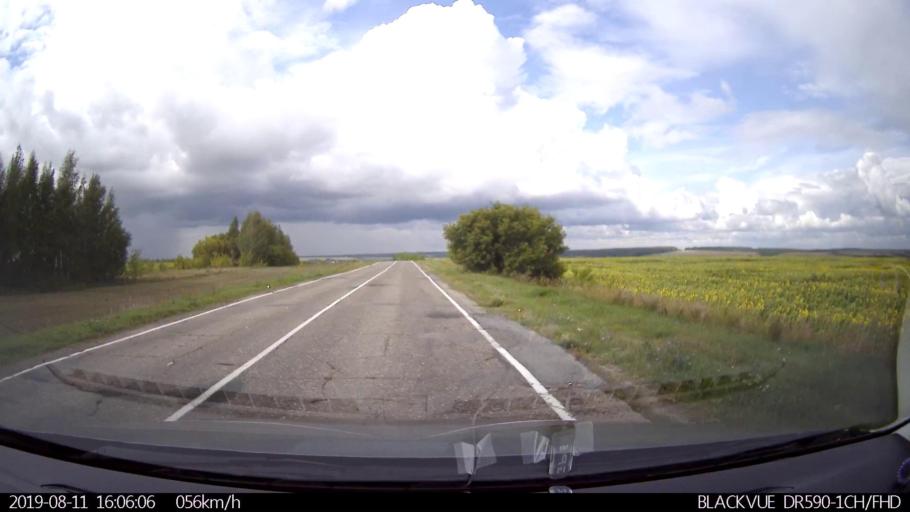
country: RU
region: Ulyanovsk
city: Ignatovka
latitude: 53.9659
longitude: 47.6492
